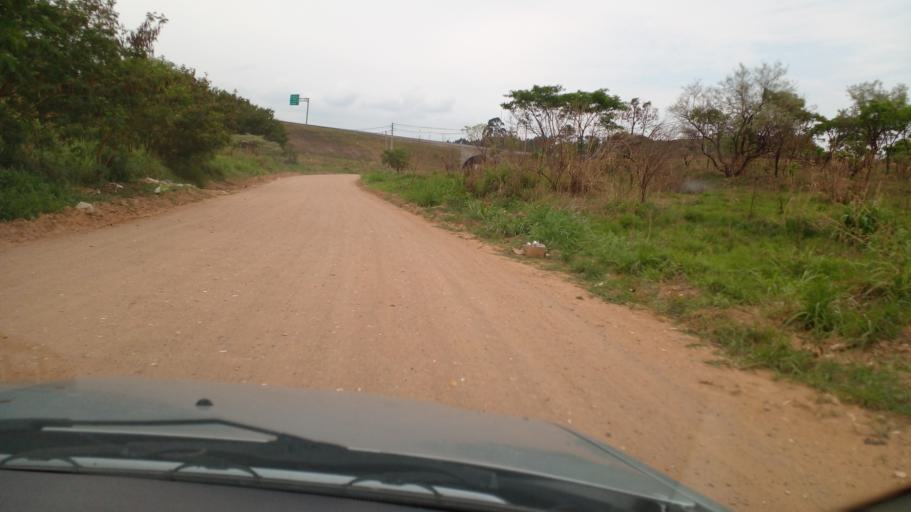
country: BR
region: Sao Paulo
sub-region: Jundiai
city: Jundiai
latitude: -23.1509
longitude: -46.8793
